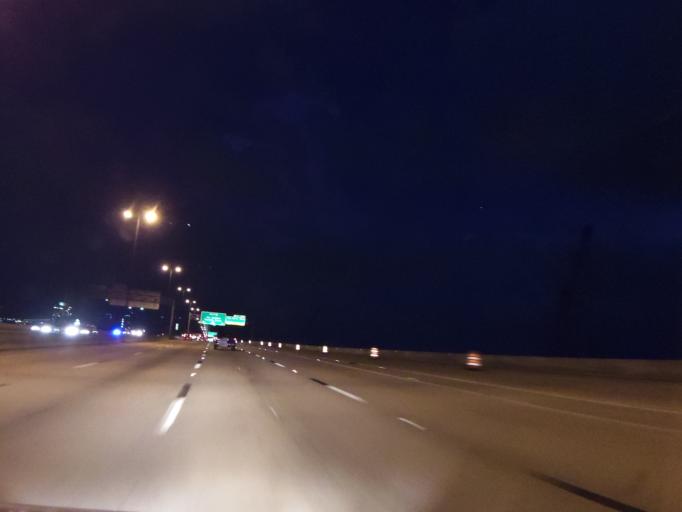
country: US
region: Florida
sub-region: Duval County
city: Jacksonville
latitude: 30.3166
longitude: -81.6731
